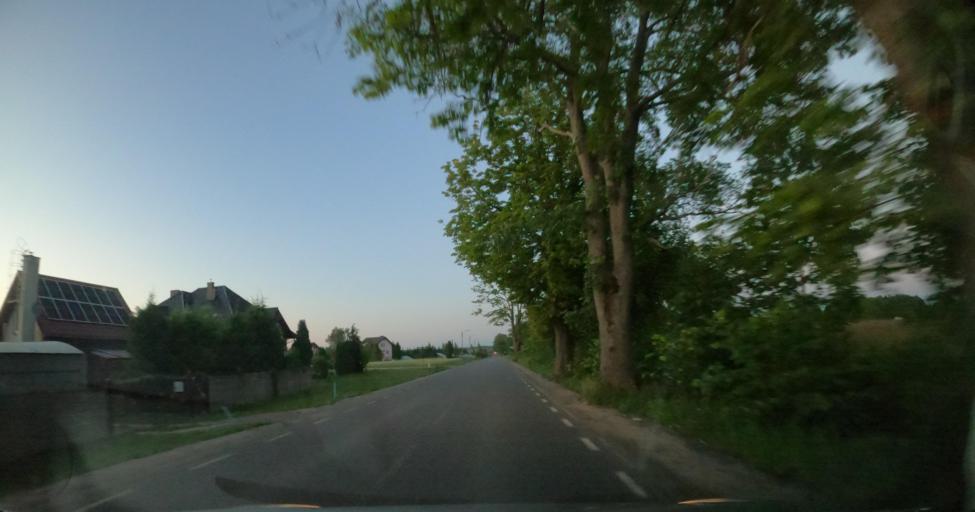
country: PL
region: Pomeranian Voivodeship
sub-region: Powiat wejherowski
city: Szemud
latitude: 54.4812
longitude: 18.2038
